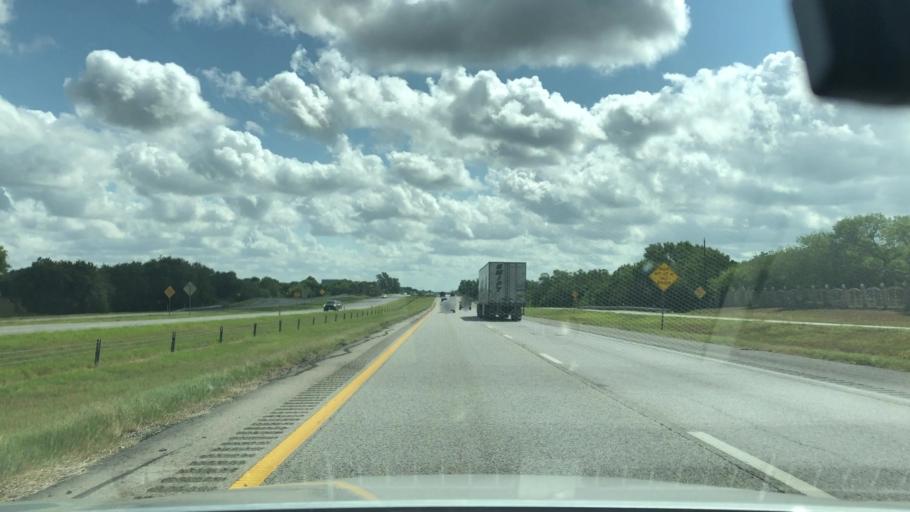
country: US
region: Texas
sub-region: Guadalupe County
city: Cibolo
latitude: 29.4993
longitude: -98.1909
